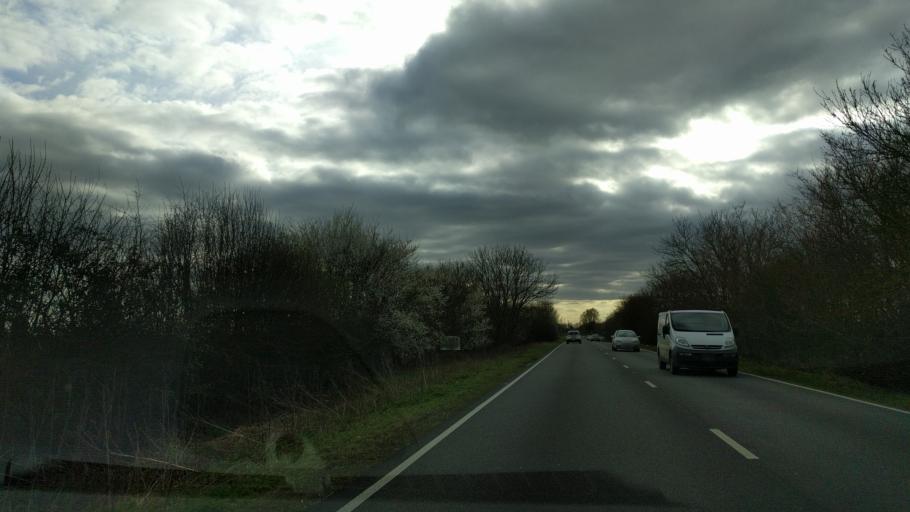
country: GB
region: England
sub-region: Cambridgeshire
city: Hemingford Grey
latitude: 52.3565
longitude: -0.1290
